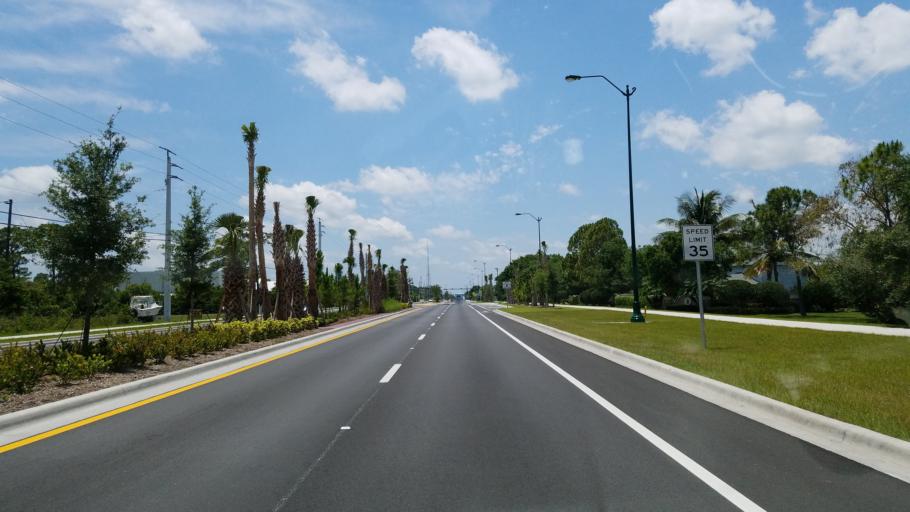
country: US
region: Florida
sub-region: Martin County
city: Palm City
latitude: 27.1613
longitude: -80.2872
